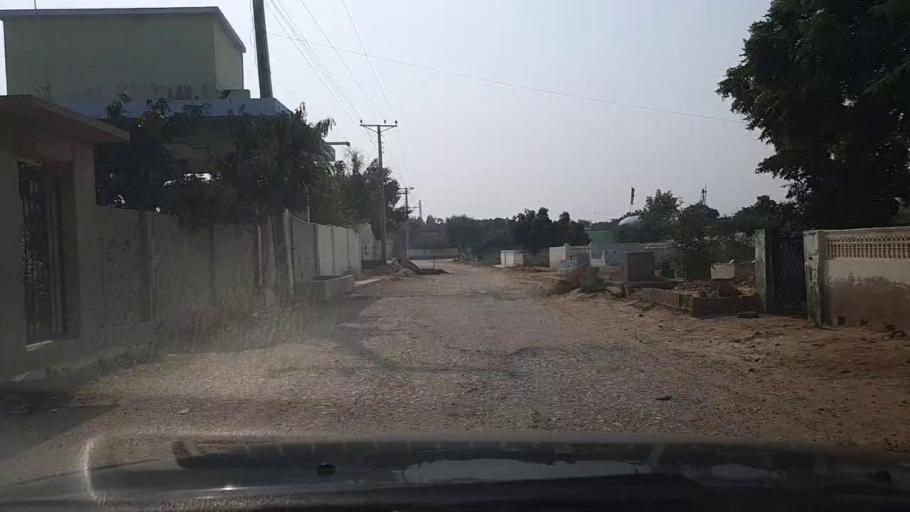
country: PK
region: Sindh
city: Thatta
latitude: 24.7467
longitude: 67.8984
